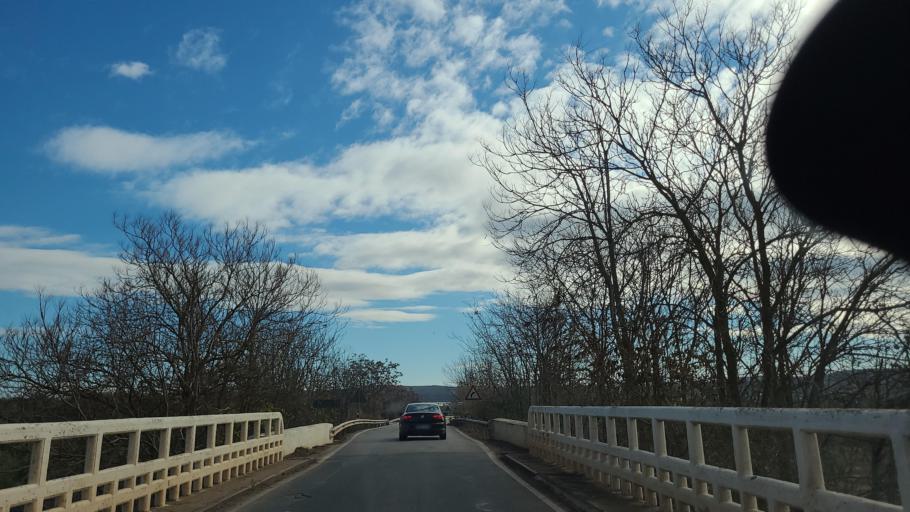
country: ES
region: Andalusia
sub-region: Provincia de Jaen
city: Villanueva de la Reina
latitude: 38.0253
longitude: -3.9150
